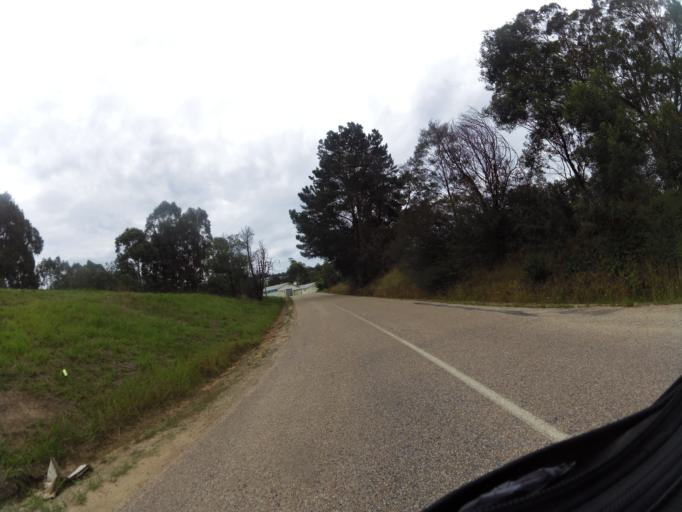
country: AU
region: Victoria
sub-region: East Gippsland
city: Lakes Entrance
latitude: -37.7055
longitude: 147.8234
